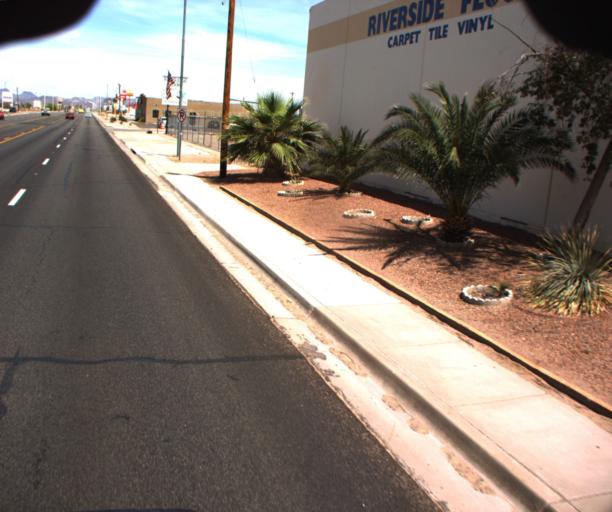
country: US
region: Arizona
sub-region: La Paz County
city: Parker
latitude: 34.1532
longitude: -114.2824
